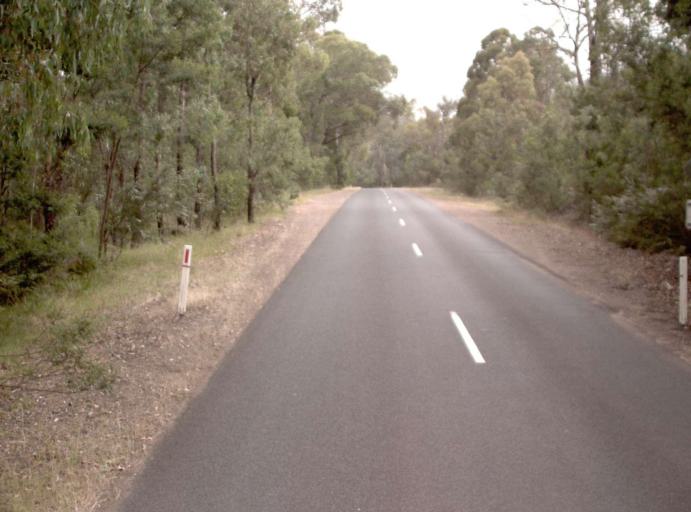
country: AU
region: Victoria
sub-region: Wellington
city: Heyfield
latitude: -37.7524
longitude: 146.6691
